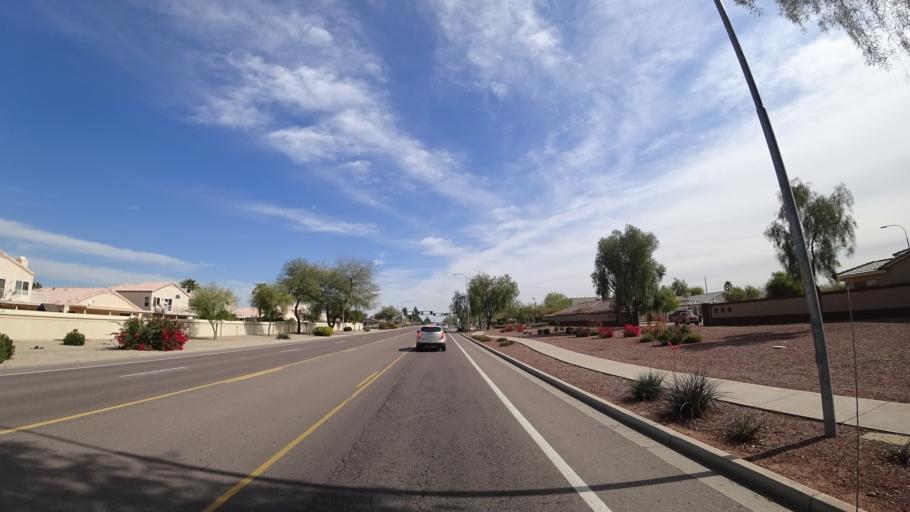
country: US
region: Arizona
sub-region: Maricopa County
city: Tolleson
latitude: 33.4789
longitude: -112.2920
